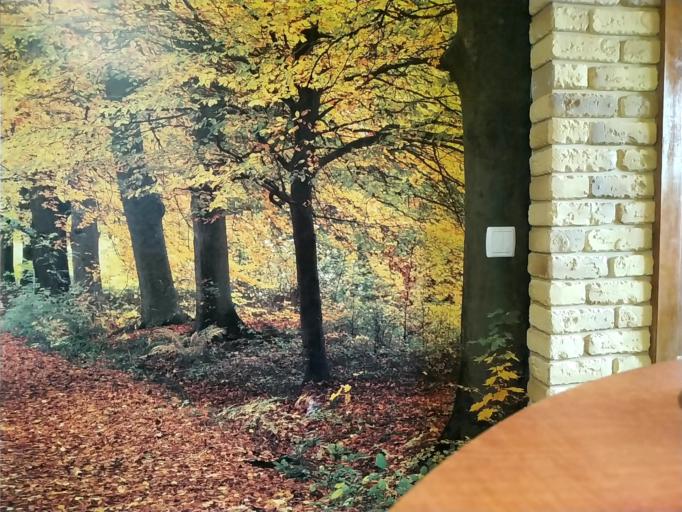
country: RU
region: Novgorod
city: Opechenskiy Posad
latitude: 58.2672
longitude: 34.0260
